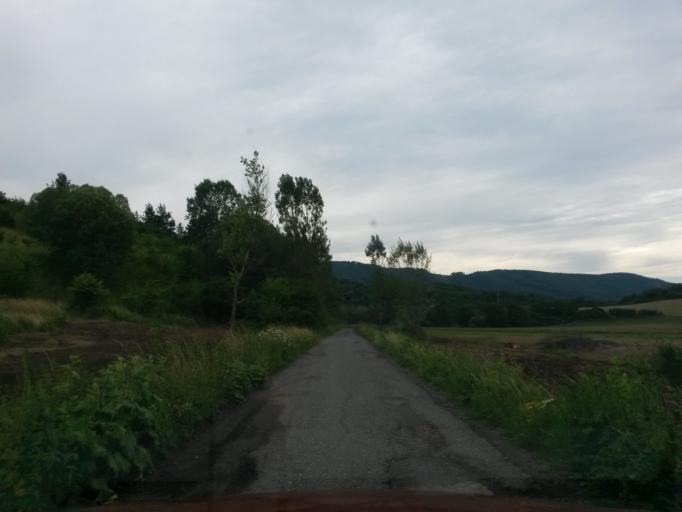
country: SK
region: Banskobystricky
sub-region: Okres Banska Bystrica
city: Zvolen
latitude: 48.5591
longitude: 19.2379
